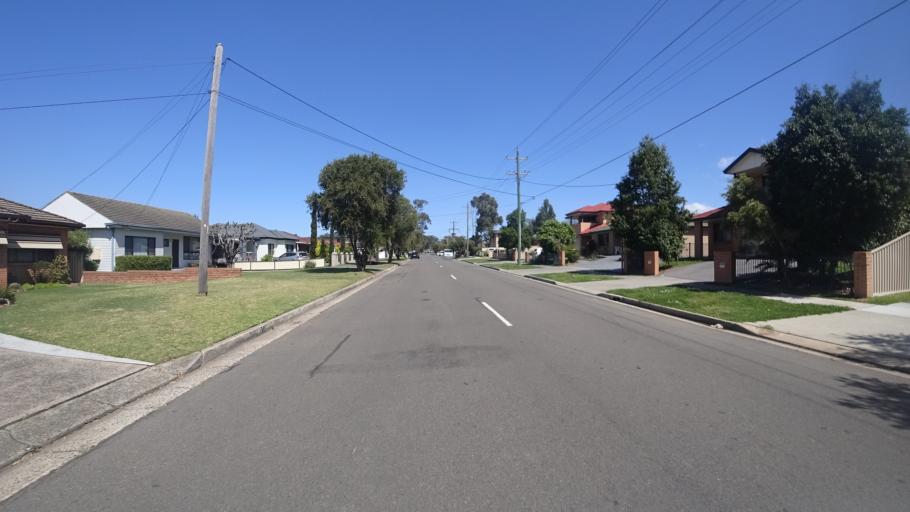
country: AU
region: New South Wales
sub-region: Liverpool
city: Miller
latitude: -33.9363
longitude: 150.8993
